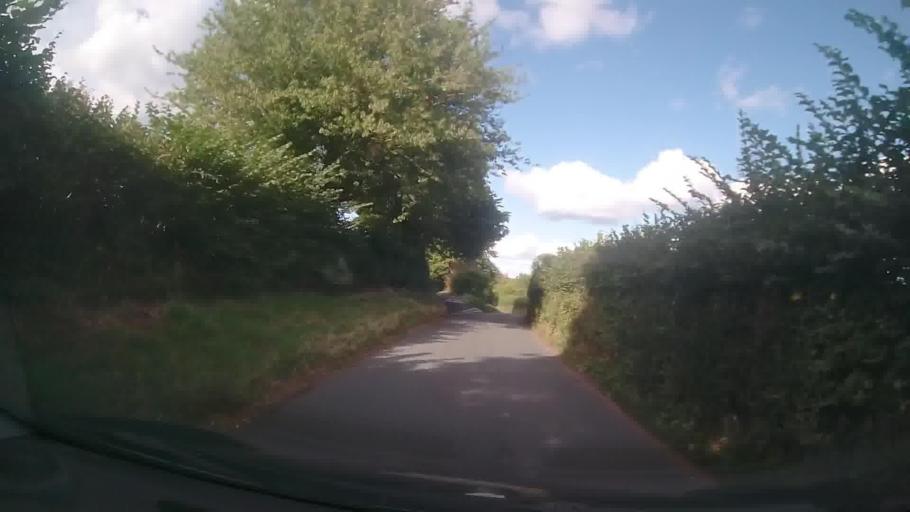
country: GB
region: Wales
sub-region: Sir Powys
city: Brecon
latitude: 51.8920
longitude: -3.2990
